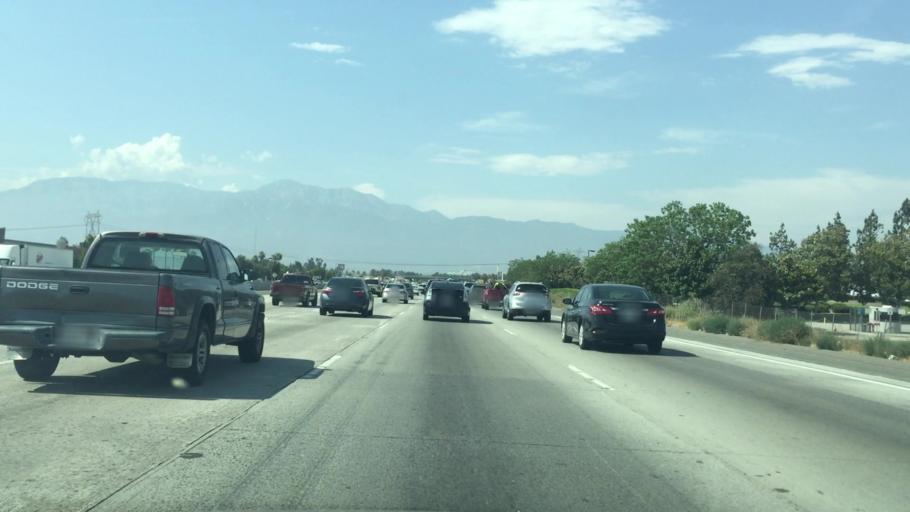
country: US
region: California
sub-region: Riverside County
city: Mira Loma
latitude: 34.0380
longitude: -117.5500
